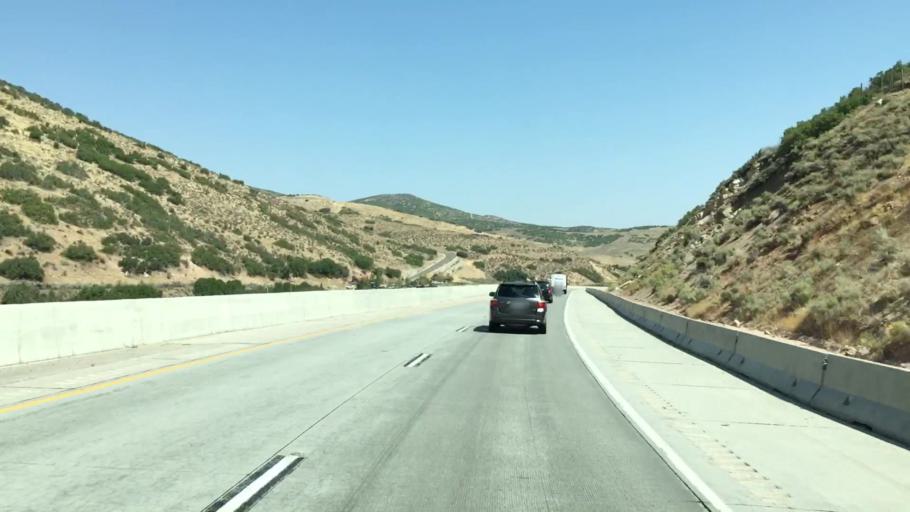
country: US
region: Utah
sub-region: Summit County
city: Coalville
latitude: 40.7956
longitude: -111.4498
